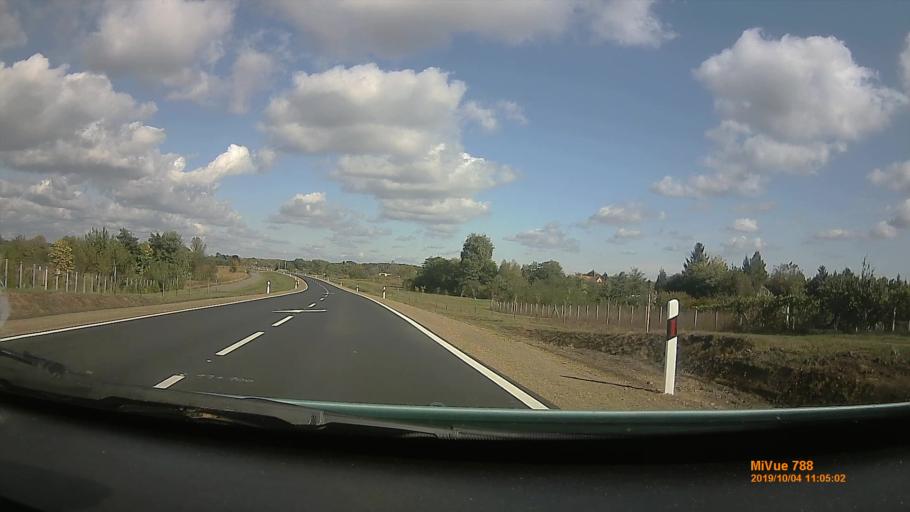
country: HU
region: Szabolcs-Szatmar-Bereg
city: Nyirtelek
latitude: 47.9920
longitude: 21.6732
